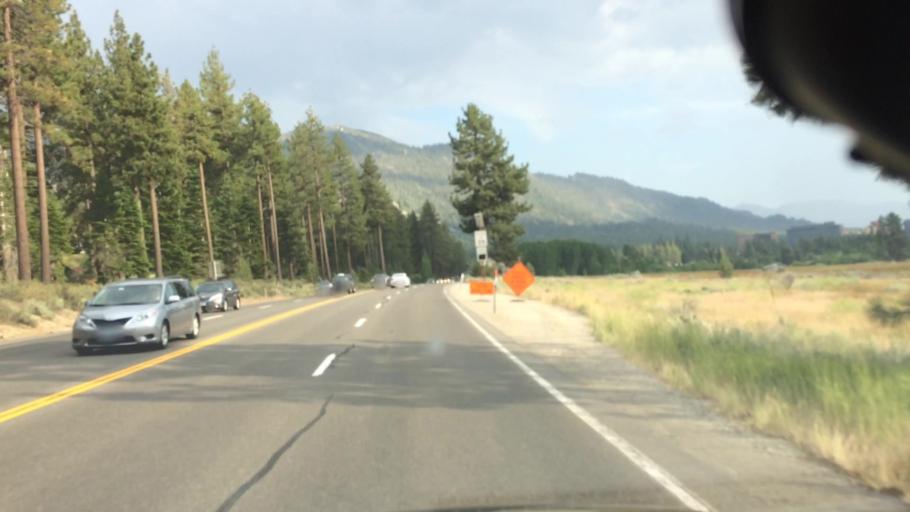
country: US
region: Nevada
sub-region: Douglas County
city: Kingsbury
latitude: 38.9779
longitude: -119.9365
